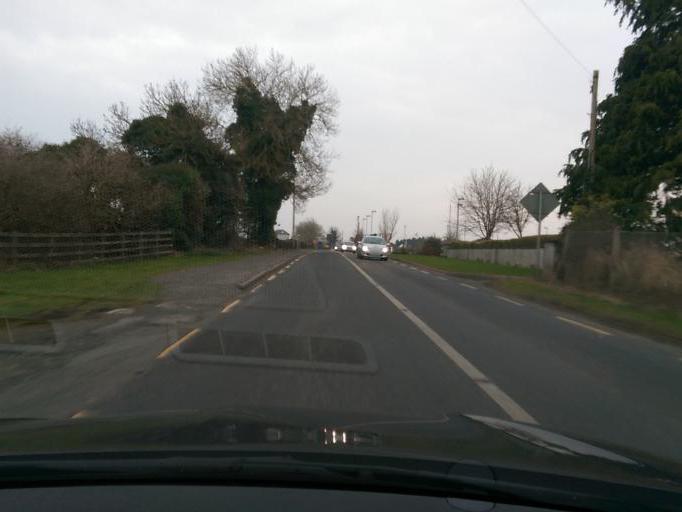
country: IE
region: Leinster
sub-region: An Longfort
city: Ballymahon
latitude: 53.5353
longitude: -7.7927
